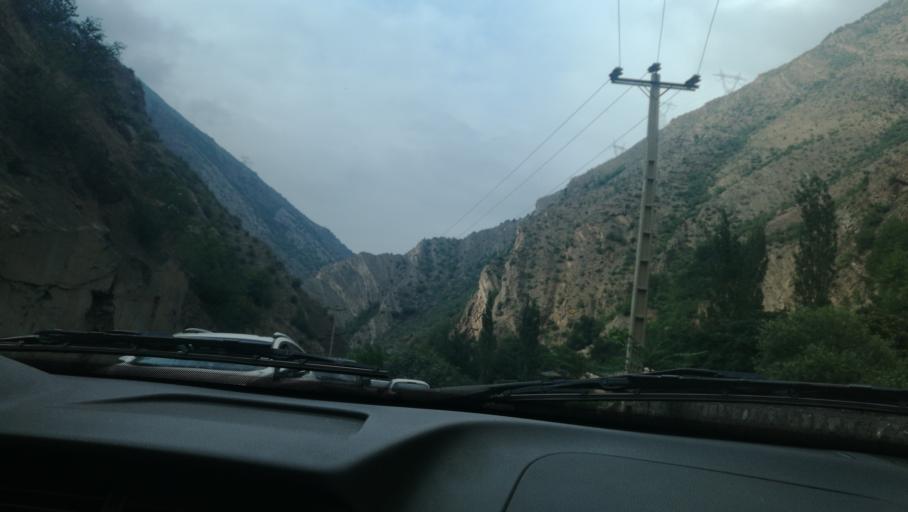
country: IR
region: Mazandaran
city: Chalus
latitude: 36.3087
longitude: 51.2477
